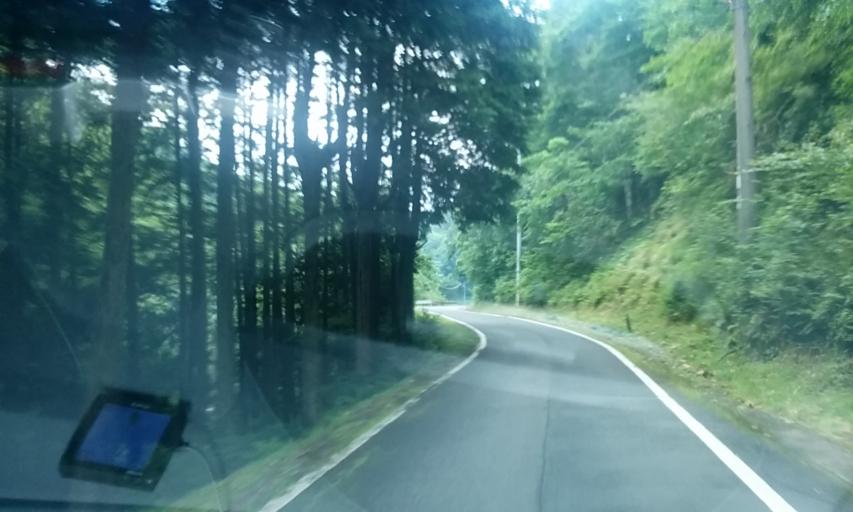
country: JP
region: Hyogo
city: Sasayama
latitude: 35.1829
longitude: 135.2168
